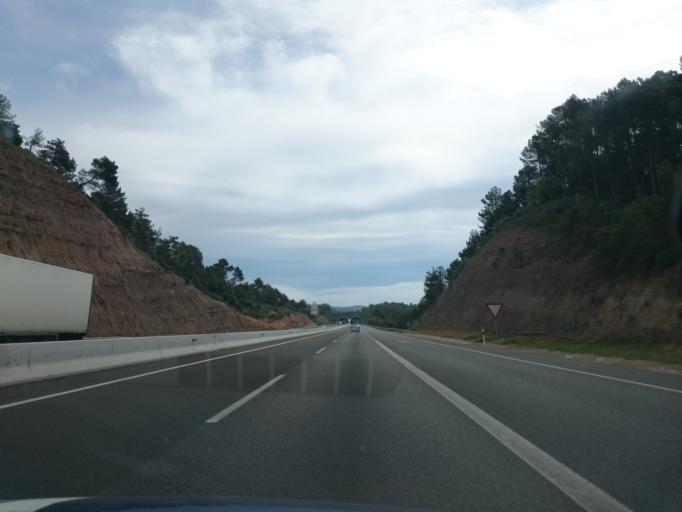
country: ES
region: Catalonia
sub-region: Provincia de Barcelona
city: Orista
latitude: 41.9028
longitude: 2.0951
